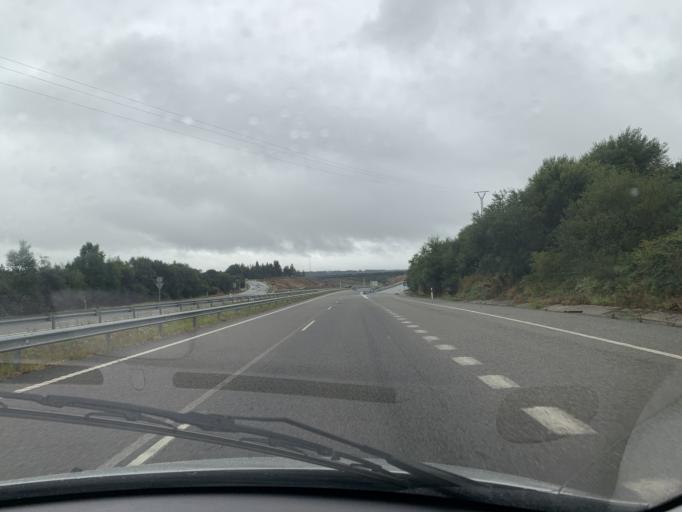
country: ES
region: Galicia
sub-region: Provincia de Lugo
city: Abadin
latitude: 43.3430
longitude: -7.5415
